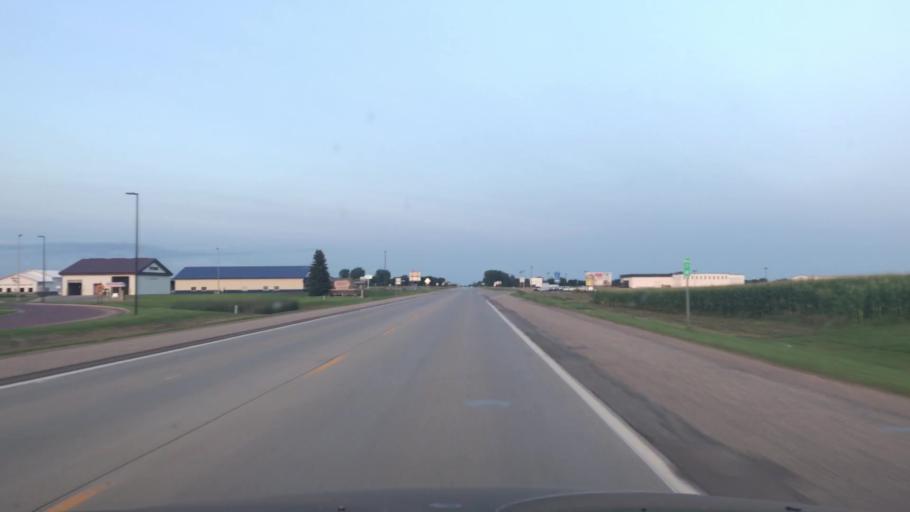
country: US
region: Minnesota
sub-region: Redwood County
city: Redwood Falls
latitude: 44.5414
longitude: -95.0807
